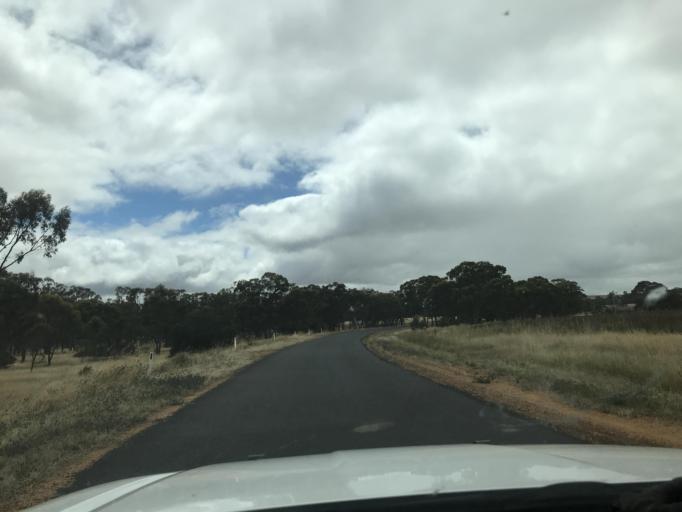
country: AU
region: South Australia
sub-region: Tatiara
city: Bordertown
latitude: -36.3156
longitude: 141.3716
